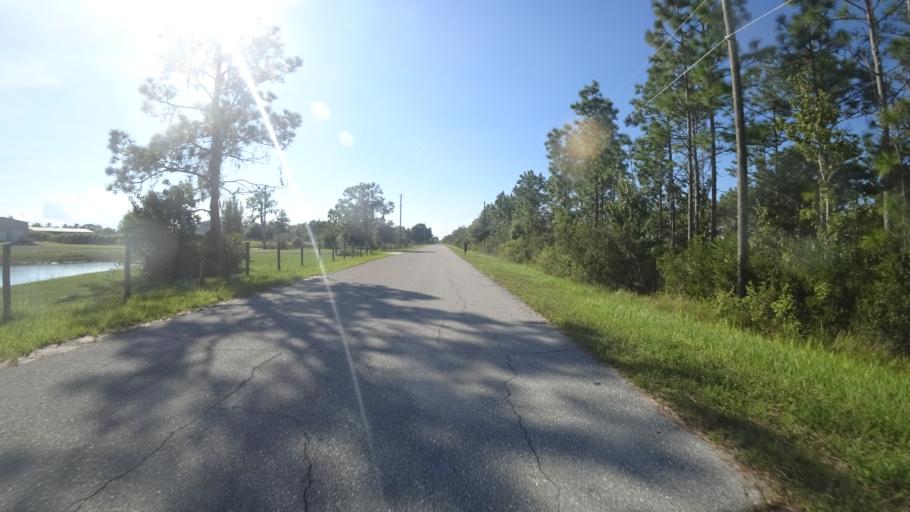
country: US
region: Florida
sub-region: Sarasota County
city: Fruitville
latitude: 27.4051
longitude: -82.2815
